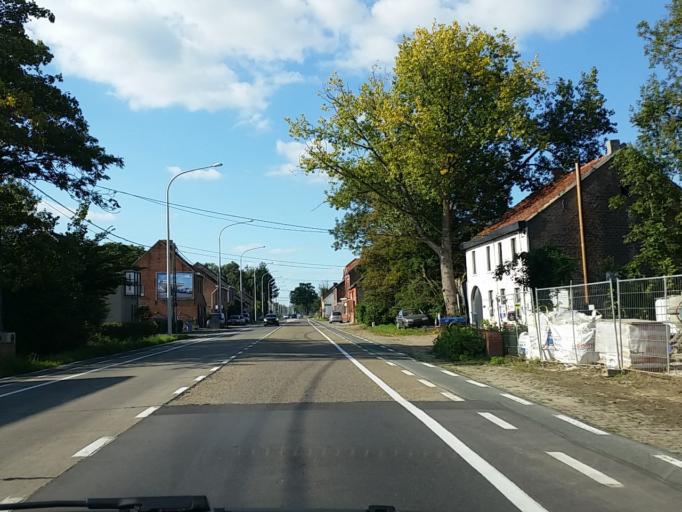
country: BE
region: Flanders
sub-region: Provincie Vlaams-Brabant
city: Herent
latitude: 50.9230
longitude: 4.6441
